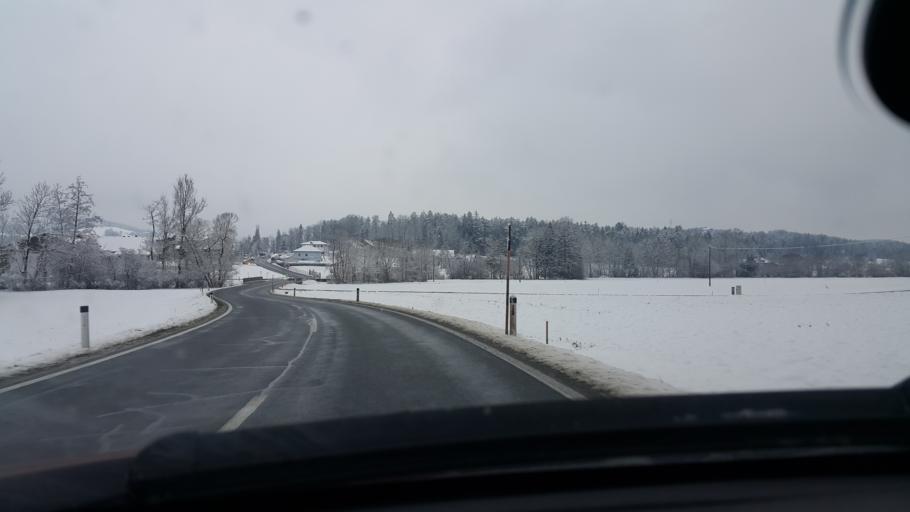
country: AT
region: Styria
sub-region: Politischer Bezirk Graz-Umgebung
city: Hitzendorf
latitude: 47.0515
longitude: 15.2921
